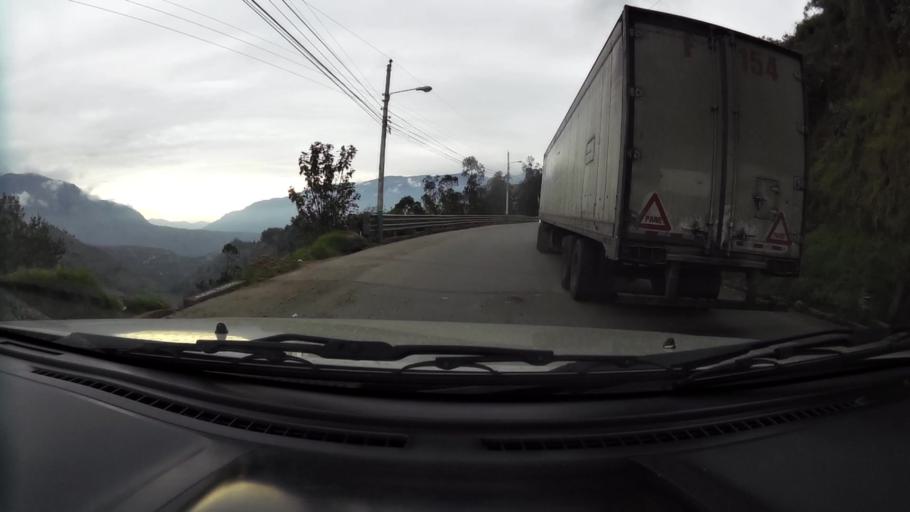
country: EC
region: Chimborazo
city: Alausi
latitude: -2.2943
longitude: -78.9117
